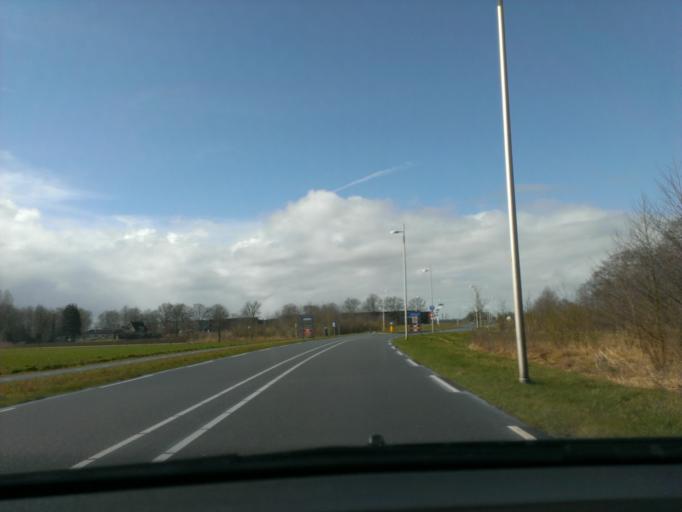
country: NL
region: Gelderland
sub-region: Gemeente Apeldoorn
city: Apeldoorn
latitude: 52.2467
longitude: 5.9821
